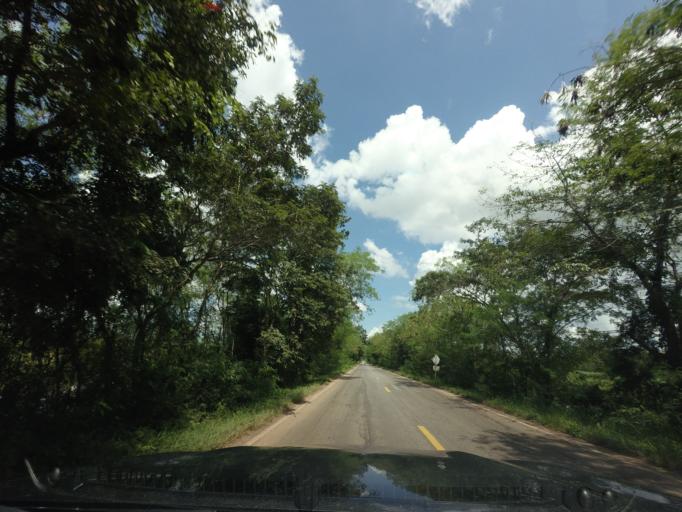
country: TH
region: Changwat Udon Thani
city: Ban Dung
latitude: 17.6718
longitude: 103.1718
